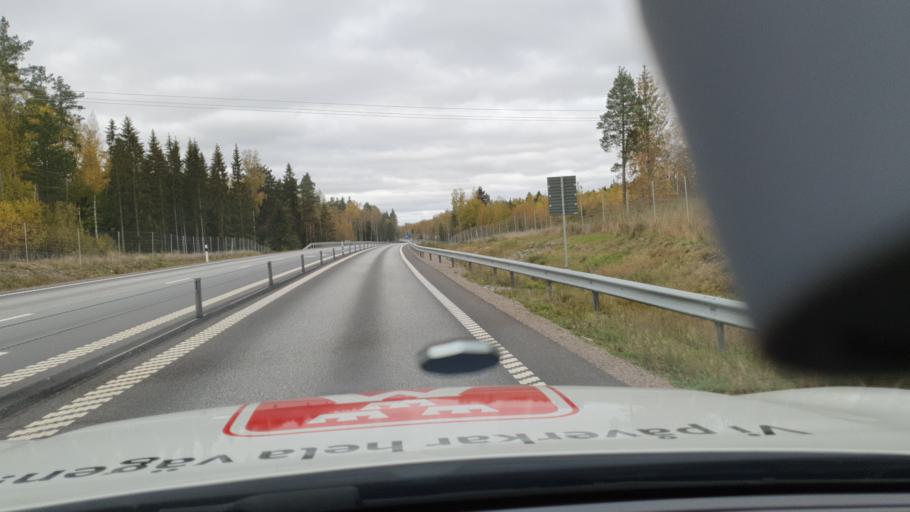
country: SE
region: OErebro
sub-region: Hallsbergs Kommun
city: Skollersta
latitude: 59.1214
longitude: 15.2921
